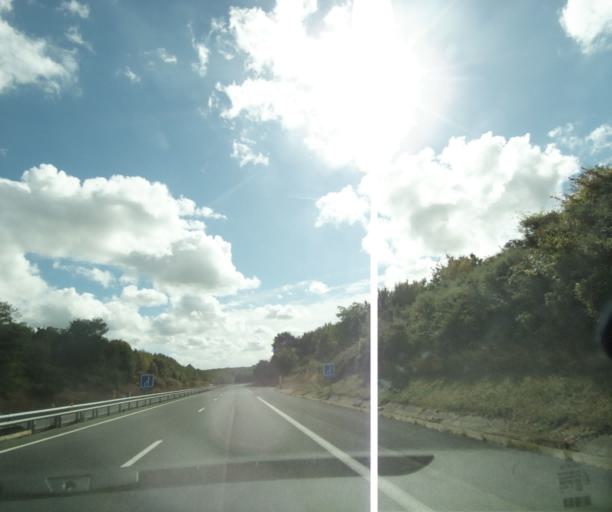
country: FR
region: Poitou-Charentes
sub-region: Departement de la Charente-Maritime
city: Bussac-sur-Charente
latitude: 45.7983
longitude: -0.6738
